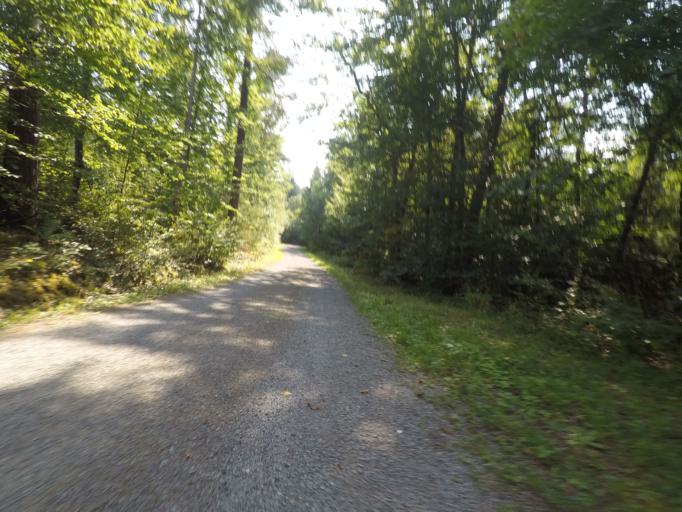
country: DE
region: Baden-Wuerttemberg
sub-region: Regierungsbezirk Stuttgart
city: Schonaich
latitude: 48.6435
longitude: 9.0775
